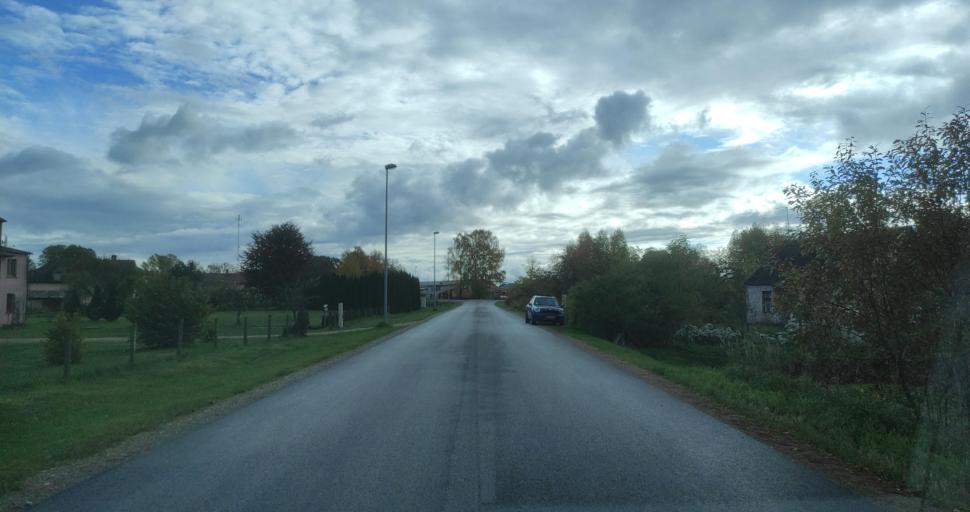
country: LV
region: Skrunda
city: Skrunda
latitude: 56.6827
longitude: 22.0136
